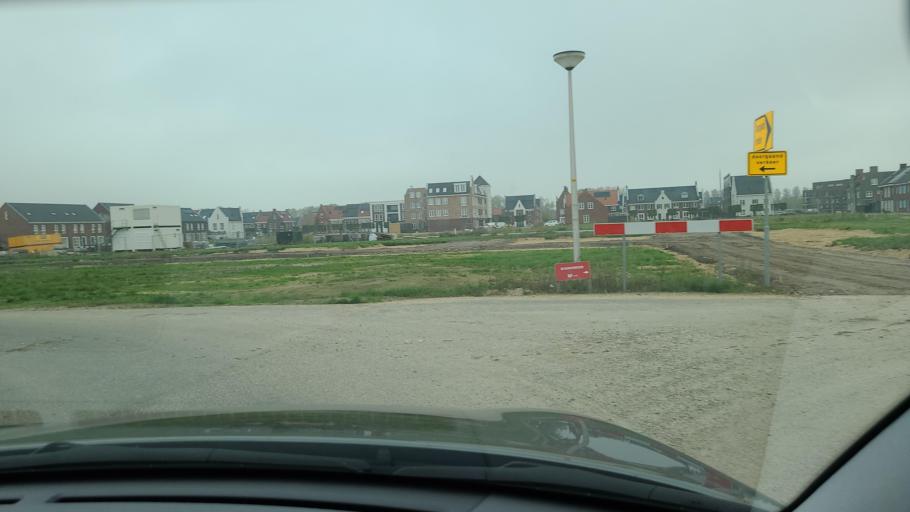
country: NL
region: Gelderland
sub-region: Gemeente Geldermalsen
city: Geldermalsen
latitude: 51.8671
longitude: 5.2960
